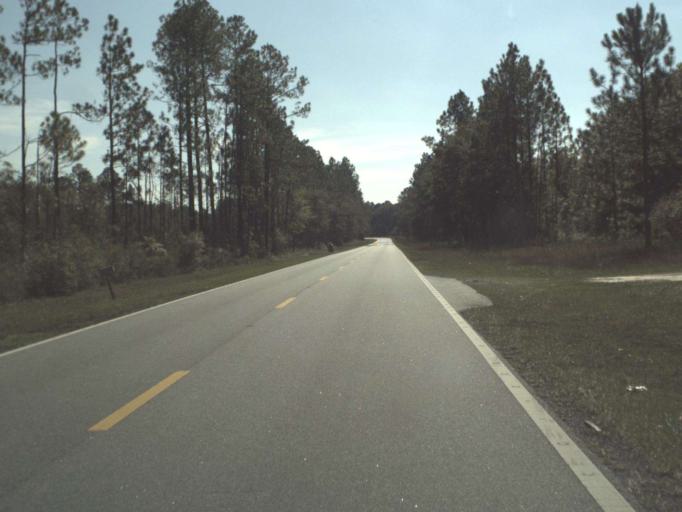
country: US
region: Florida
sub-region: Gulf County
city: Wewahitchka
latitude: 30.0347
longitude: -84.9836
